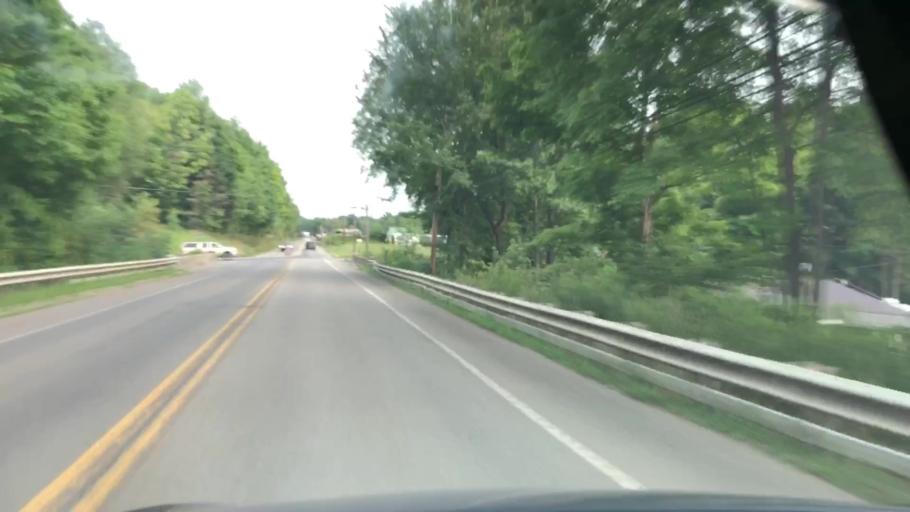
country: US
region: Pennsylvania
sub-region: Crawford County
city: Titusville
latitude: 41.6539
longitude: -79.7241
